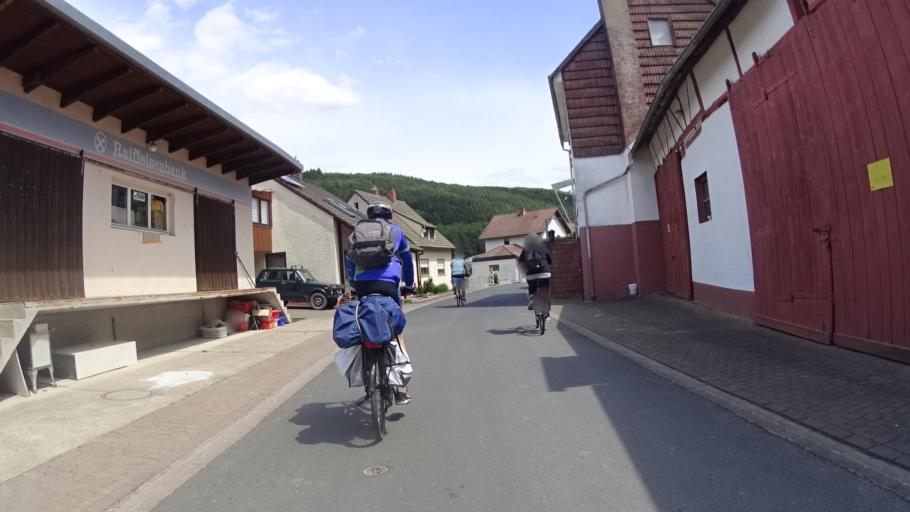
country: DE
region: Bavaria
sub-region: Regierungsbezirk Unterfranken
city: Neunkirchen
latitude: 49.6705
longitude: 9.3916
